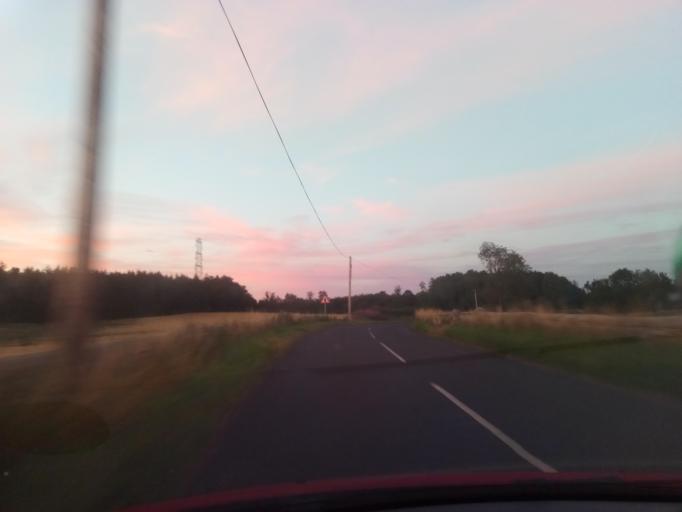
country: GB
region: England
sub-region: Northumberland
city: Wall
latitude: 55.0110
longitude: -2.1710
